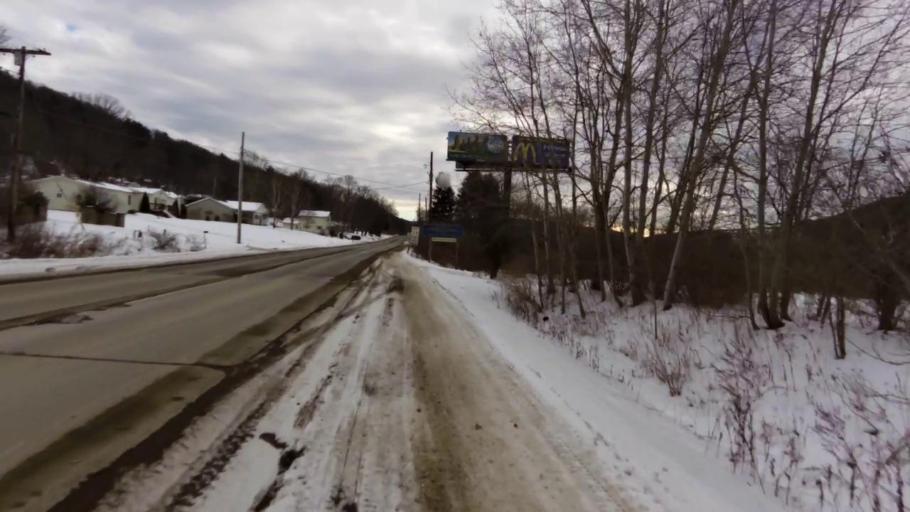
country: US
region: Pennsylvania
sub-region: McKean County
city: Foster Brook
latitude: 42.0004
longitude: -78.6181
